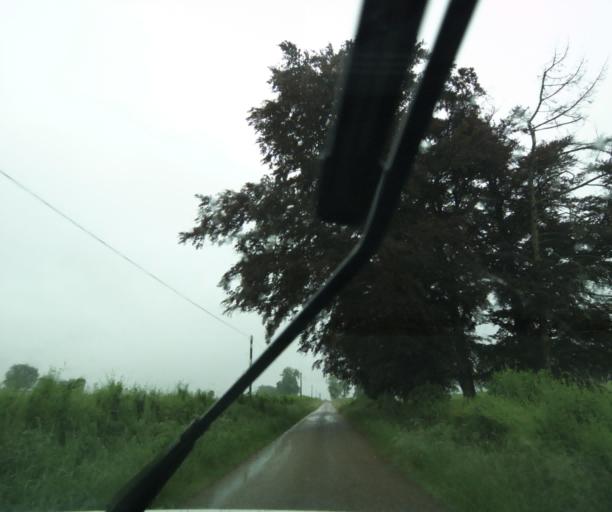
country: FR
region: Bourgogne
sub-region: Departement de Saone-et-Loire
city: Charolles
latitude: 46.4004
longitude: 4.2900
